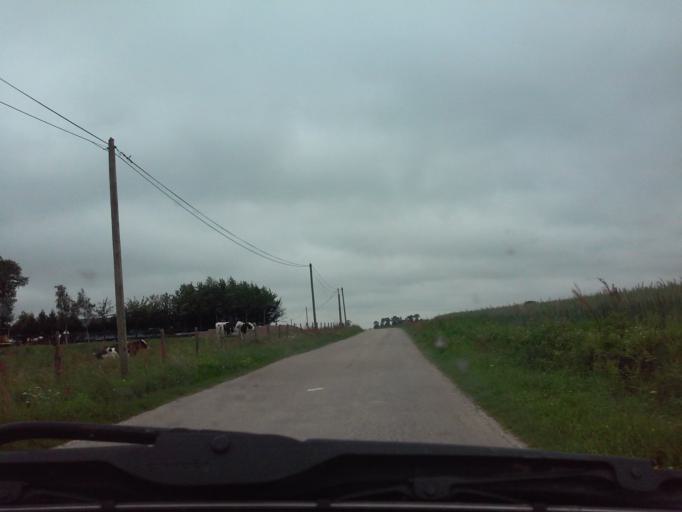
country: FR
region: Pays de la Loire
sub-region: Departement de la Mayenne
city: Ballots
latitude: 47.9603
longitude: -1.0411
